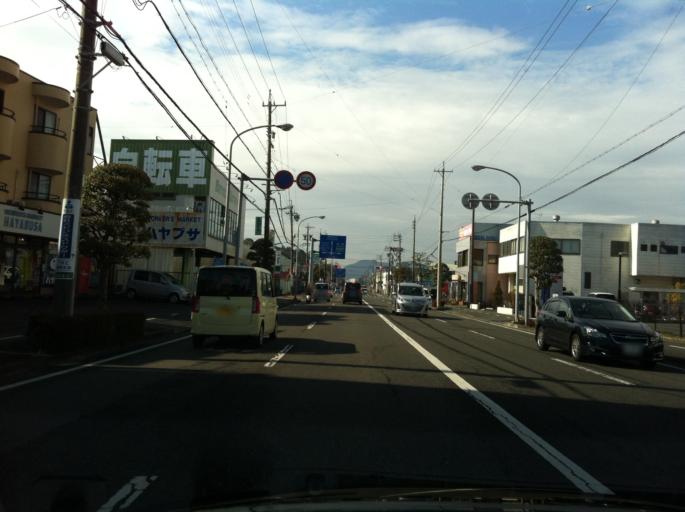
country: JP
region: Shizuoka
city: Shizuoka-shi
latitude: 35.0000
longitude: 138.4171
